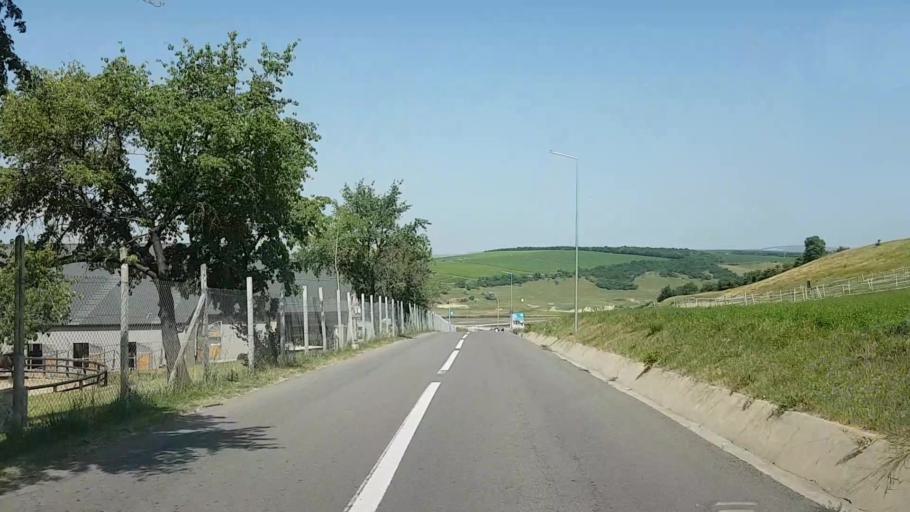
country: RO
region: Cluj
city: Turda
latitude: 46.5852
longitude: 23.7973
